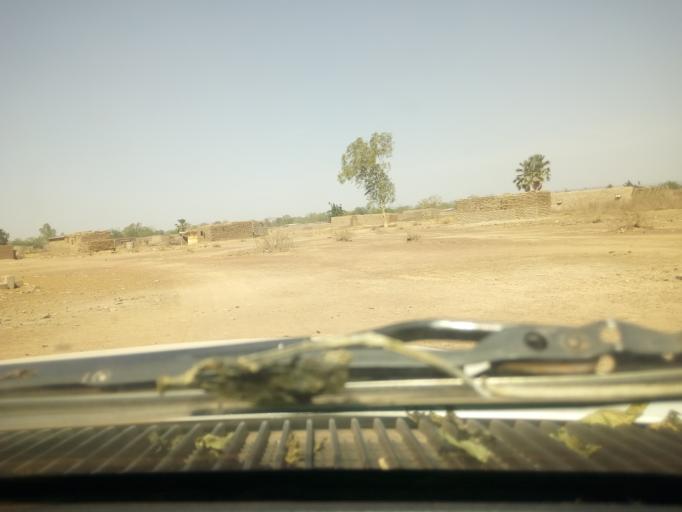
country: ML
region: Koulikoro
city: Koulikoro
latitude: 12.6476
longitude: -7.7082
